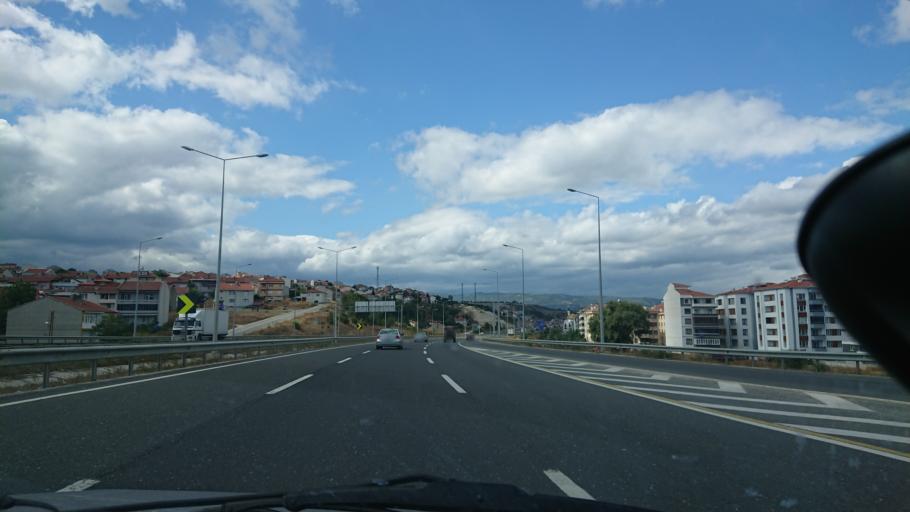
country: TR
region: Bilecik
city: Bozuyuk
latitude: 39.8968
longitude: 30.0423
